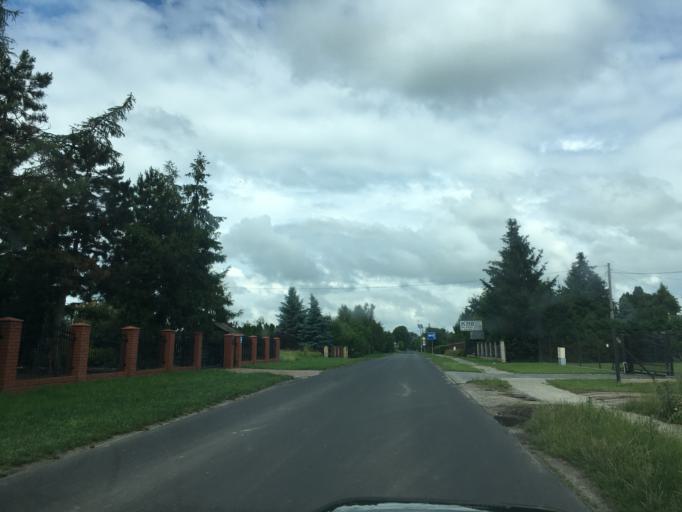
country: PL
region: Lublin Voivodeship
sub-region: Powiat swidnicki
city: Melgiew
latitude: 51.2132
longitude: 22.7482
